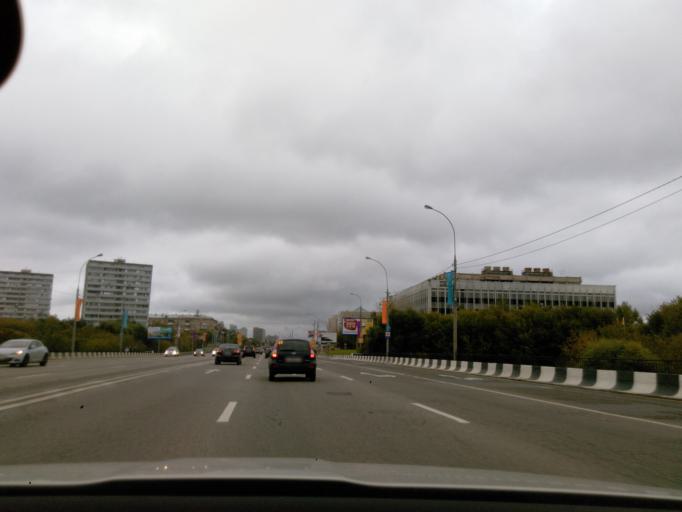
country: RU
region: Moscow
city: Strogino
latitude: 55.8277
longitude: 37.4197
